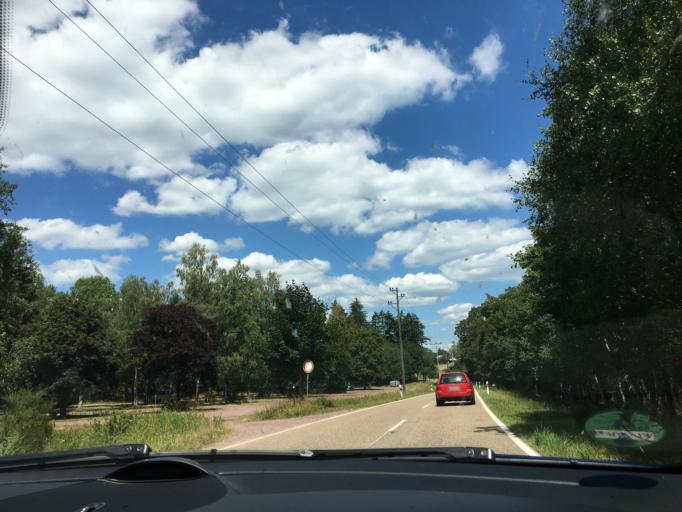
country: DE
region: Rheinland-Pfalz
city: Hauenstein
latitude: 49.2388
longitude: 7.8342
